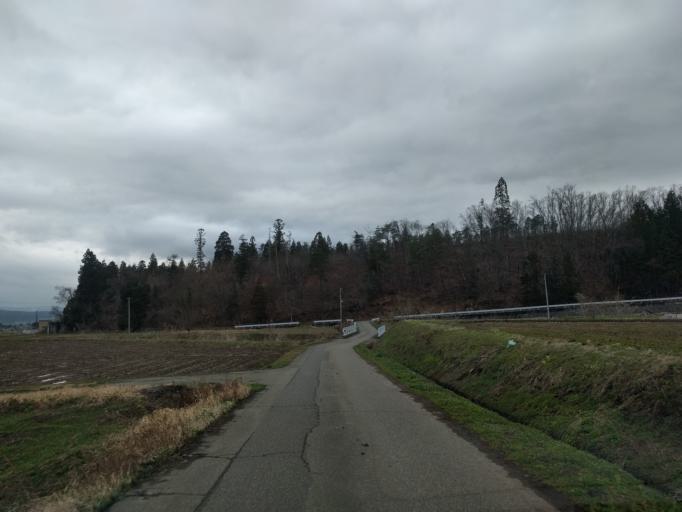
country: JP
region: Fukushima
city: Kitakata
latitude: 37.6689
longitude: 139.9167
